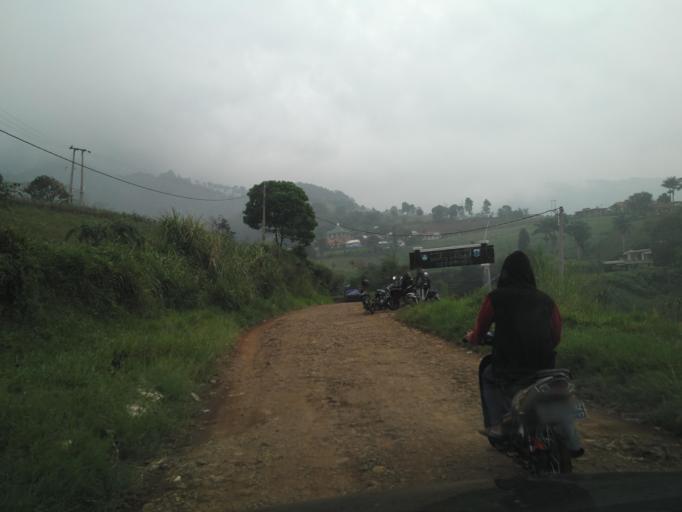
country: ID
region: West Java
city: Caringin
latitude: -6.6783
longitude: 107.0271
